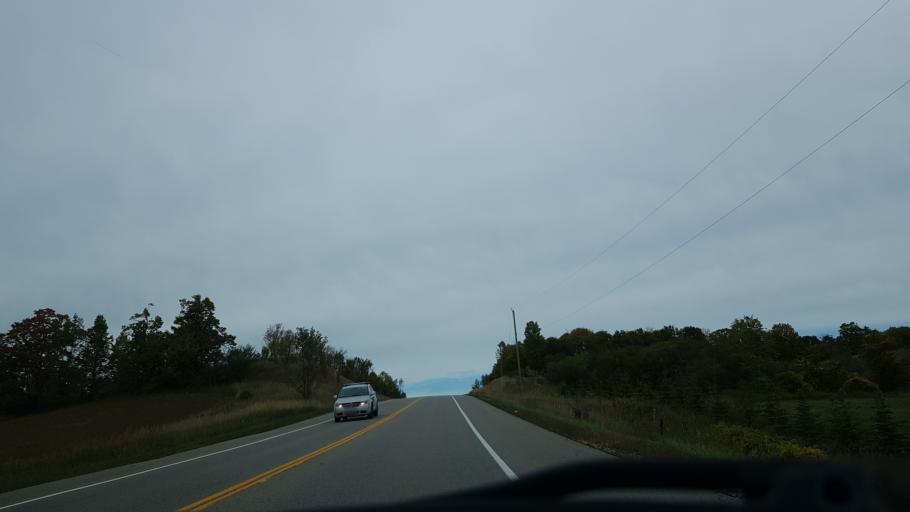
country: CA
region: Ontario
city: Orangeville
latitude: 44.0553
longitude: -80.0126
